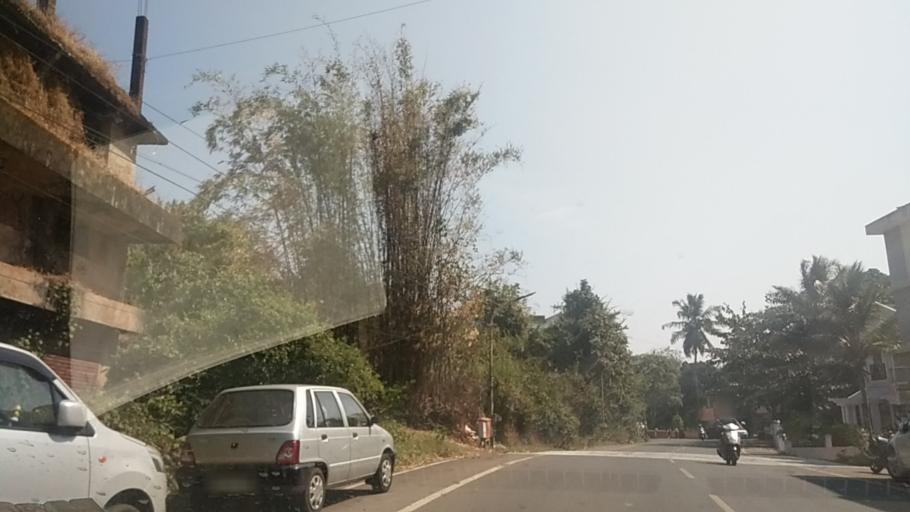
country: IN
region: Goa
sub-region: South Goa
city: Madgaon
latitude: 15.2915
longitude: 73.9580
